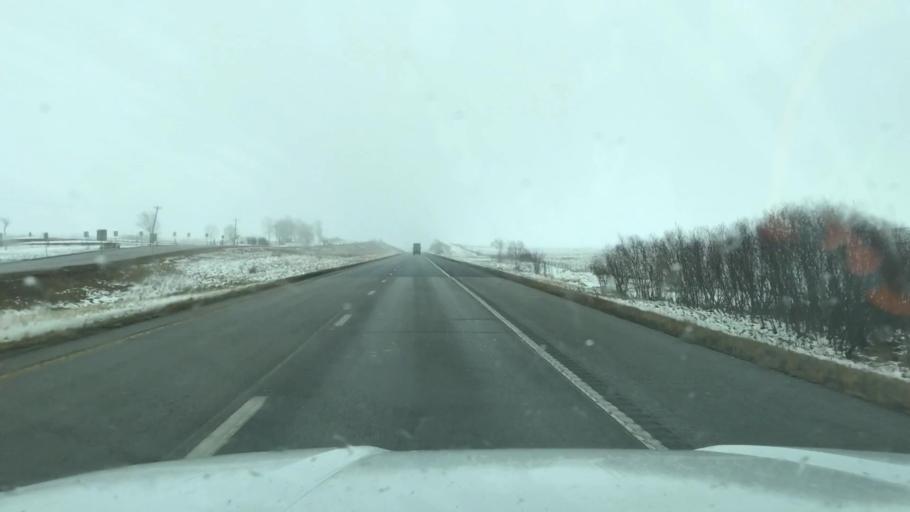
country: US
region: Missouri
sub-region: Clinton County
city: Gower
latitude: 39.7613
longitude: -94.5524
